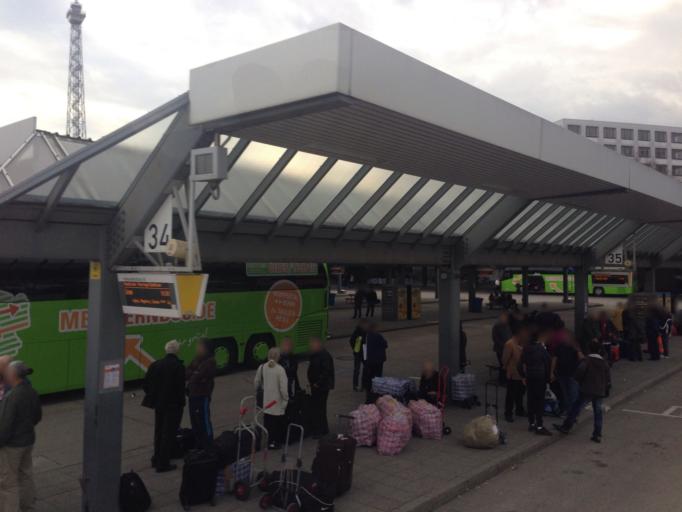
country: DE
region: Berlin
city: Charlottenburg Bezirk
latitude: 52.5078
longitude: 13.2800
